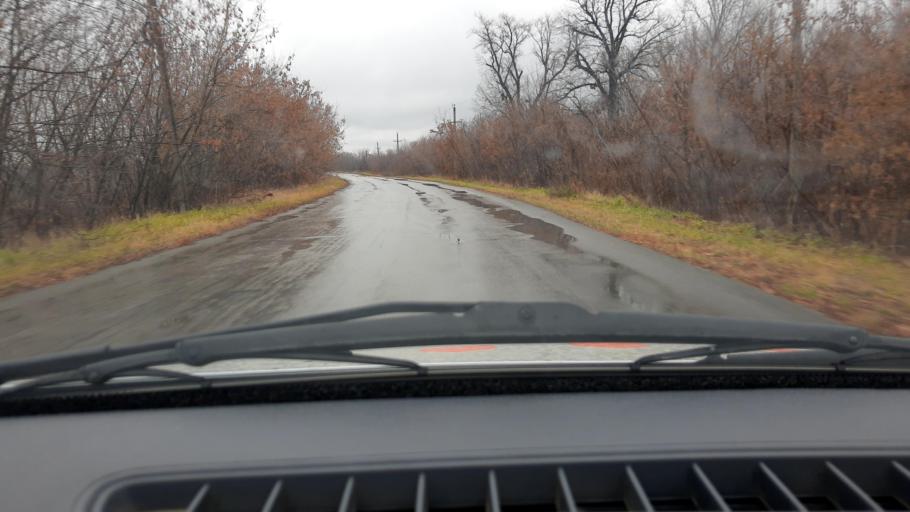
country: RU
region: Bashkortostan
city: Iglino
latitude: 54.8040
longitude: 56.1939
